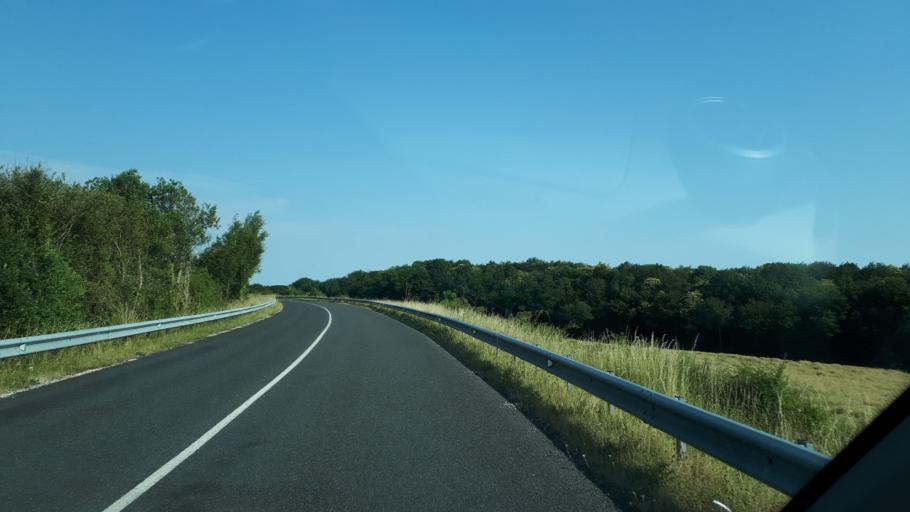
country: FR
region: Centre
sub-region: Departement du Loir-et-Cher
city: La Ville-aux-Clercs
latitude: 47.9701
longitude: 1.0485
